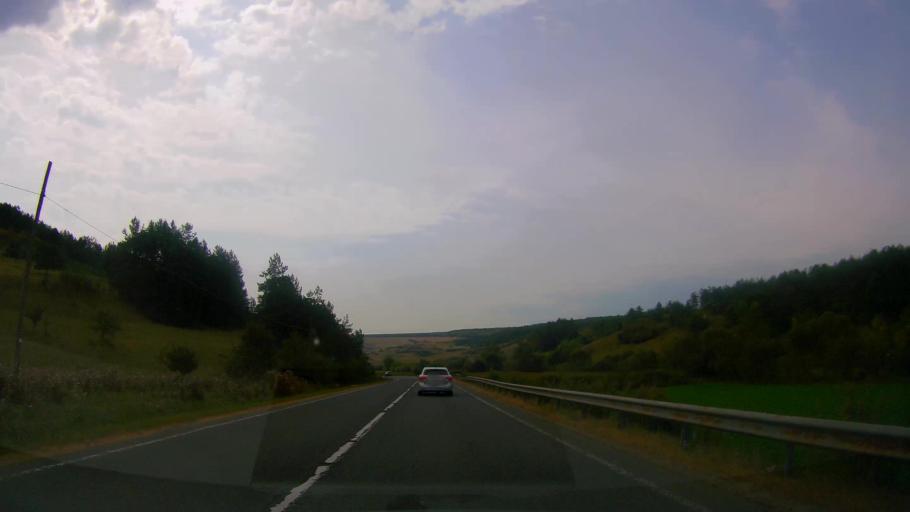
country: RO
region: Cluj
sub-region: Comuna Sanpaul
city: Sanpaul
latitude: 46.8491
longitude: 23.4050
